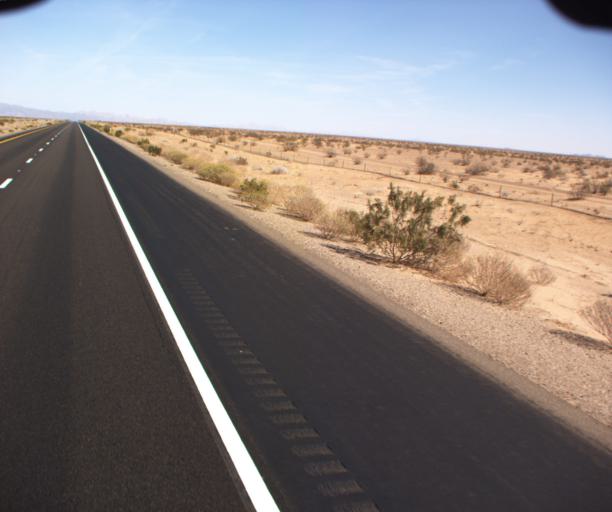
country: US
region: Arizona
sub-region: Yuma County
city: Somerton
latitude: 32.4951
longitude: -114.5964
